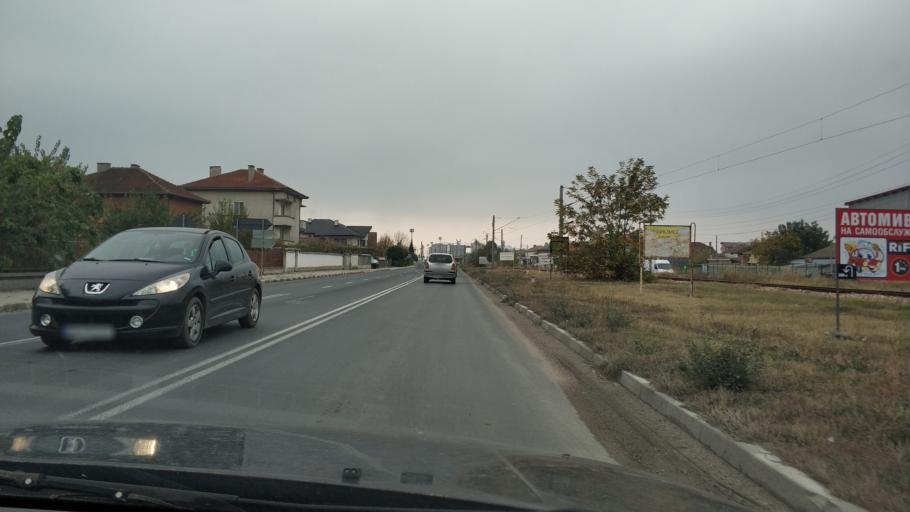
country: BG
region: Plovdiv
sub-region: Obshtina Plovdiv
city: Plovdiv
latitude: 42.2366
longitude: 24.7235
